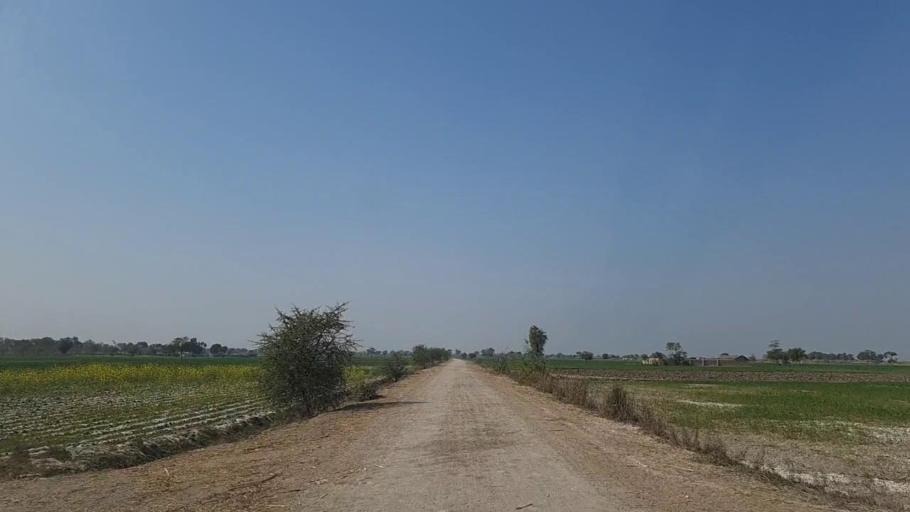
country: PK
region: Sindh
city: Daur
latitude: 26.4413
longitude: 68.2926
